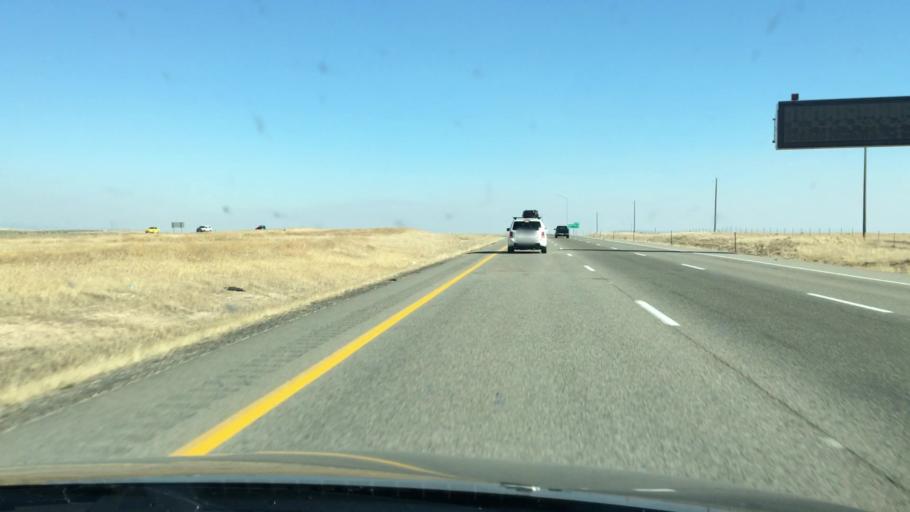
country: US
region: Idaho
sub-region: Ada County
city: Boise
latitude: 43.4714
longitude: -116.1006
